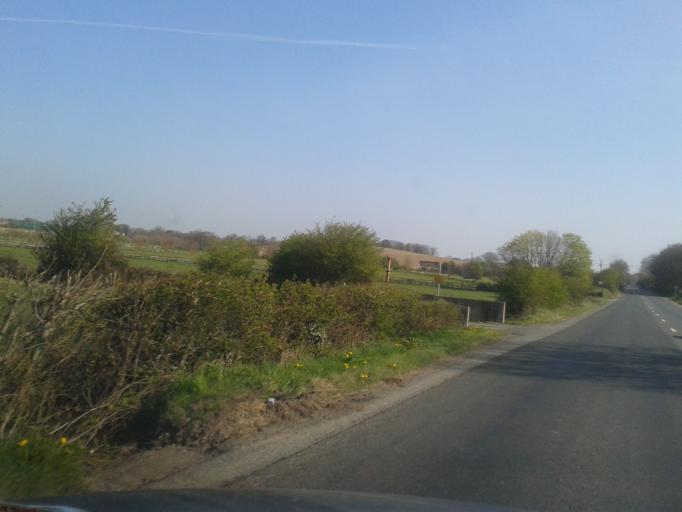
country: IE
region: Leinster
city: Balrothery
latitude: 53.5825
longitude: -6.1965
